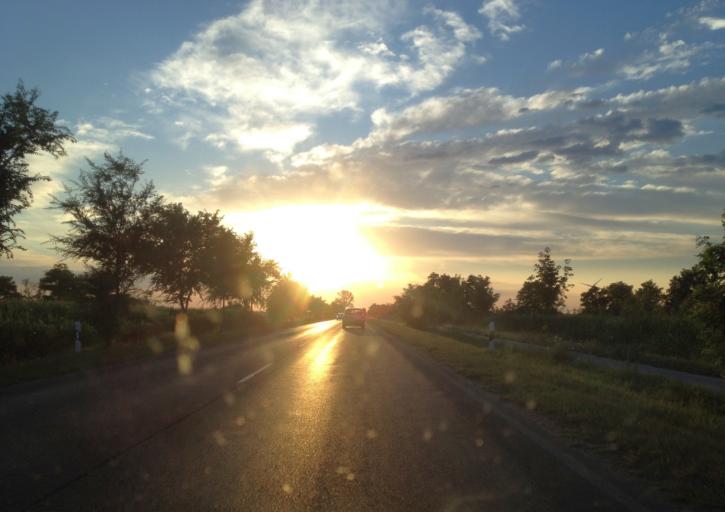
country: HU
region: Gyor-Moson-Sopron
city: Mosonmagyarovar
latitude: 47.8863
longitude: 17.2370
